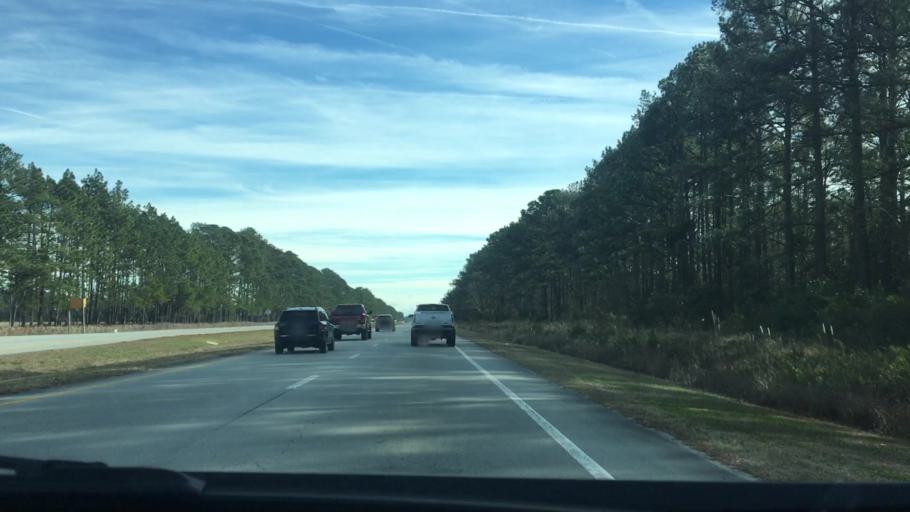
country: US
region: North Carolina
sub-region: Carteret County
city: Newport
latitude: 34.7697
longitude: -76.8642
